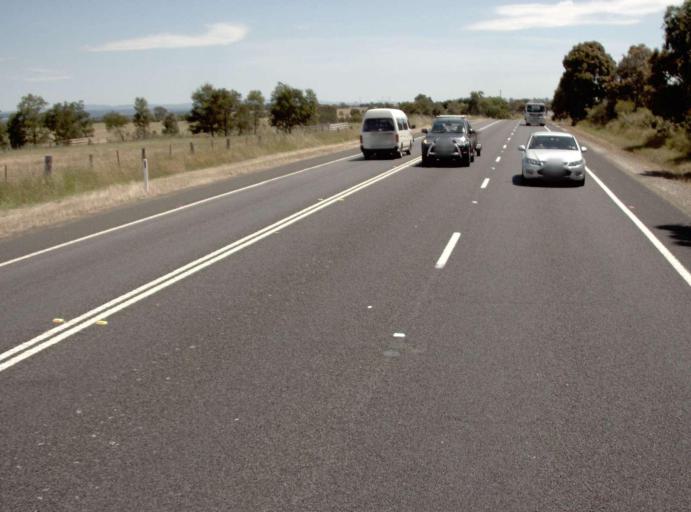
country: AU
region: Victoria
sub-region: Wellington
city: Heyfield
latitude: -38.1275
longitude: 146.8347
